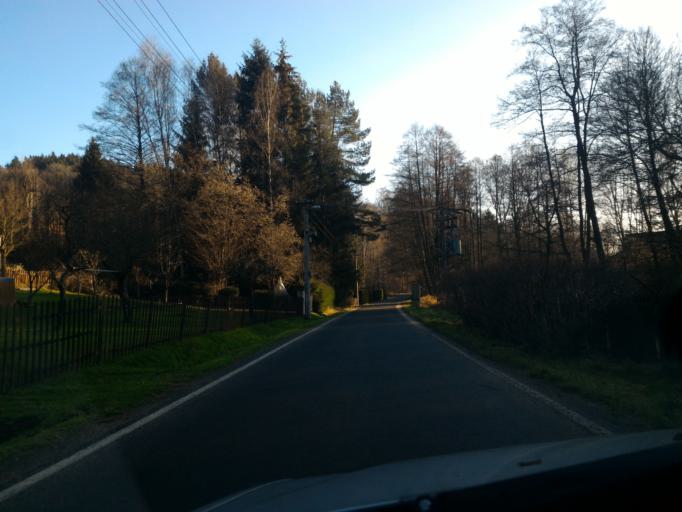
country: DE
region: Saxony
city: Kurort Oybin
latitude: 50.8026
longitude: 14.7182
